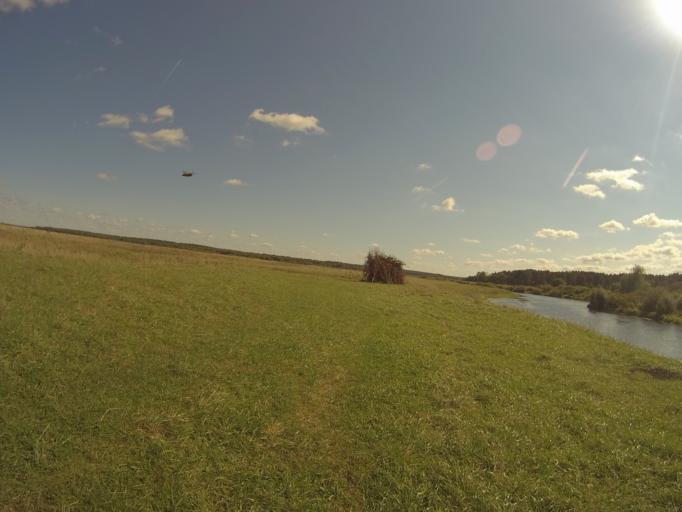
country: RU
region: Vladimir
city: Orgtrud
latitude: 56.3018
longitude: 40.6119
